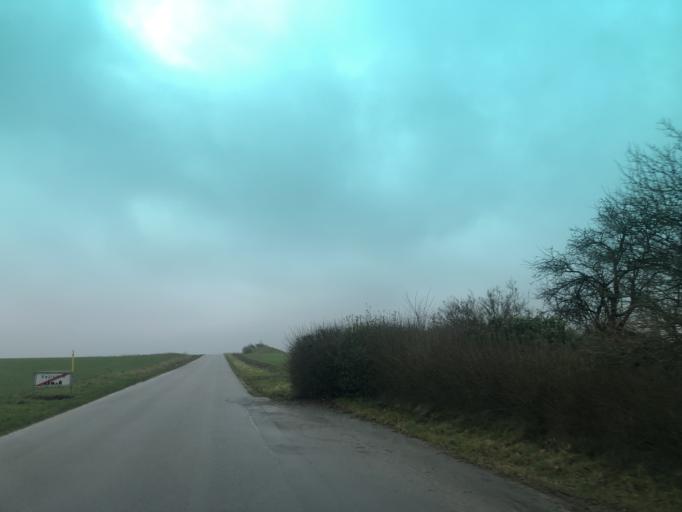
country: DK
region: Central Jutland
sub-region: Struer Kommune
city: Struer
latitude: 56.4461
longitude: 8.5880
